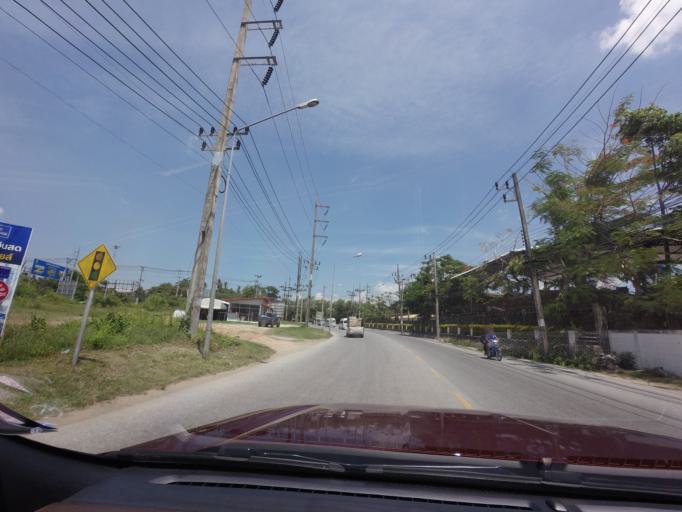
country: TH
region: Yala
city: Yala
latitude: 6.5536
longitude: 101.2708
